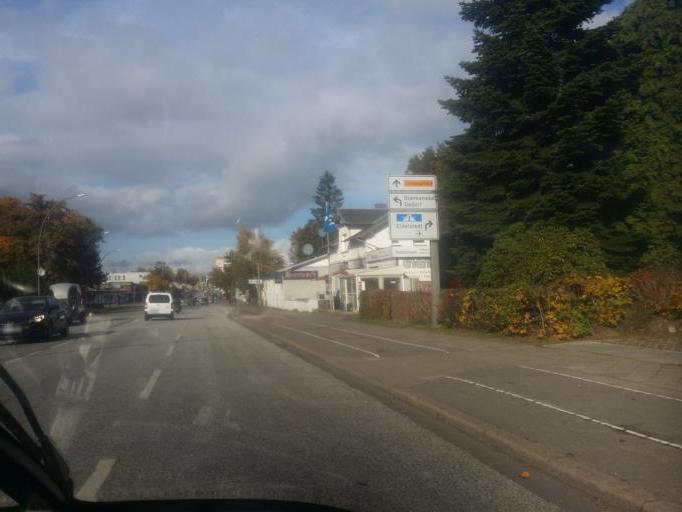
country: DE
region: Hamburg
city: Eidelstedt
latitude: 53.5872
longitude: 9.8775
